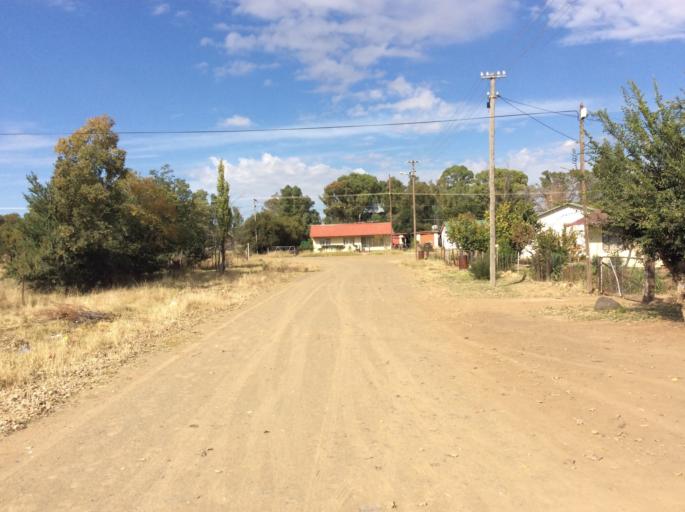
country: LS
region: Mafeteng
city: Mafeteng
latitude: -29.7293
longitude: 27.0259
